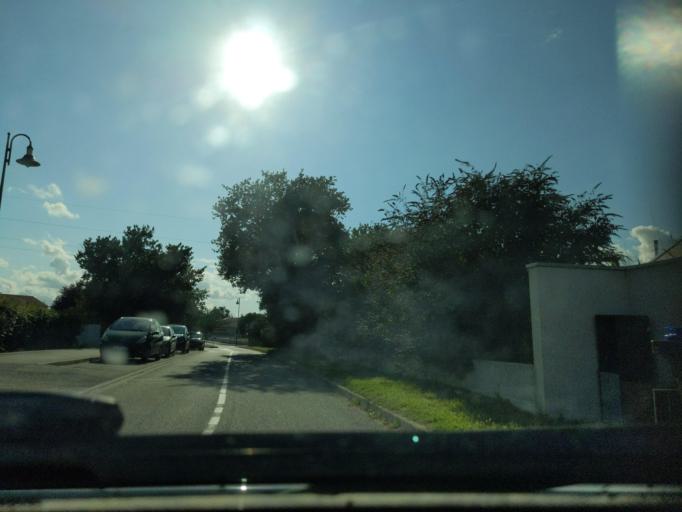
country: FR
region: Midi-Pyrenees
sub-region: Departement de la Haute-Garonne
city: Pibrac
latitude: 43.6099
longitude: 1.2761
